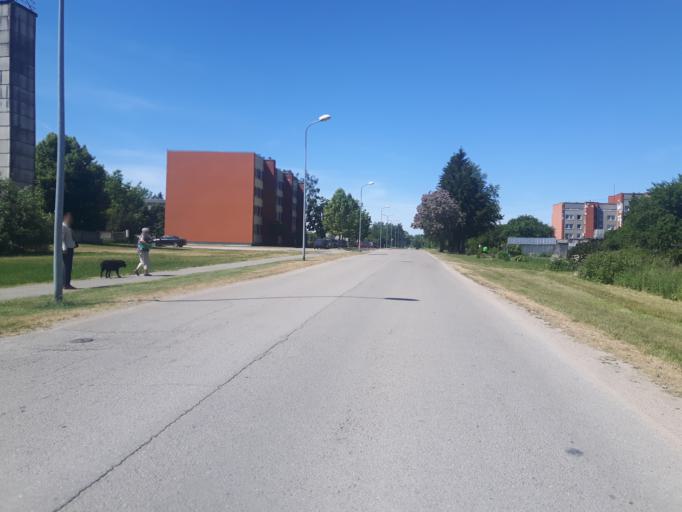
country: LV
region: Grobina
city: Grobina
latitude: 56.5377
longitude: 21.1671
